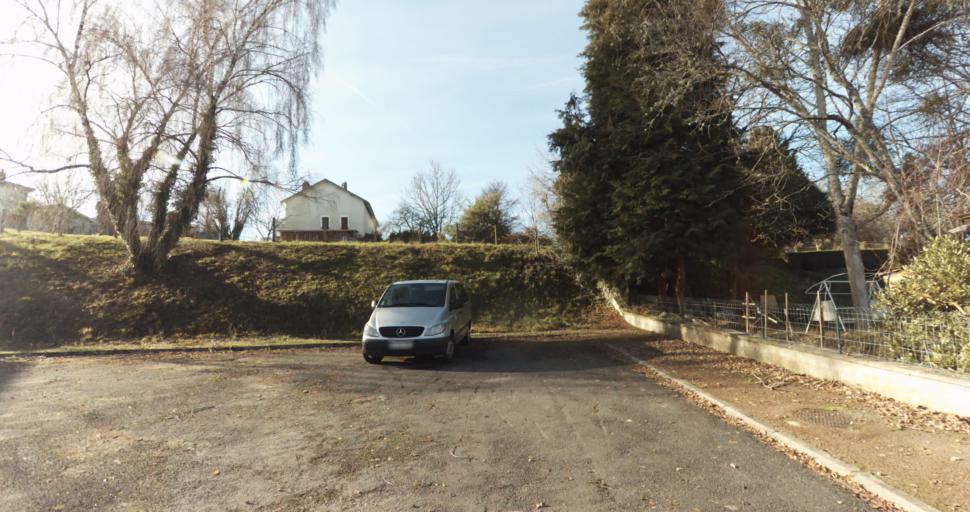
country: FR
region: Limousin
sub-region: Departement de la Haute-Vienne
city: Aixe-sur-Vienne
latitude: 45.7918
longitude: 1.1256
